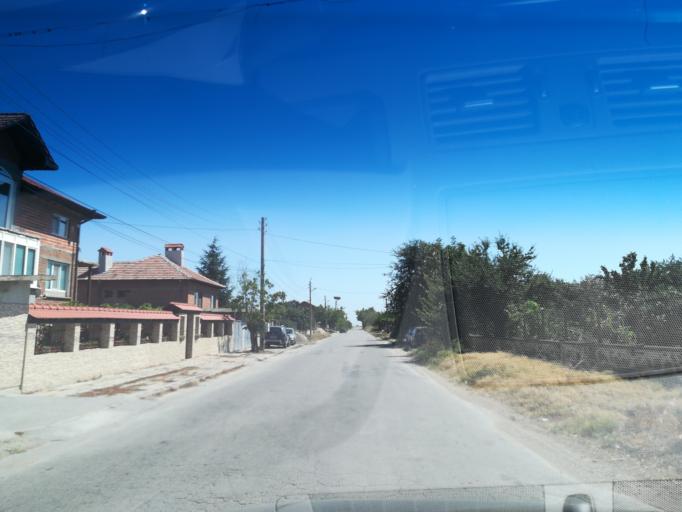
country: BG
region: Pazardzhik
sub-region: Obshtina Pazardzhik
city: Pazardzhik
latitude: 42.3292
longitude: 24.4036
